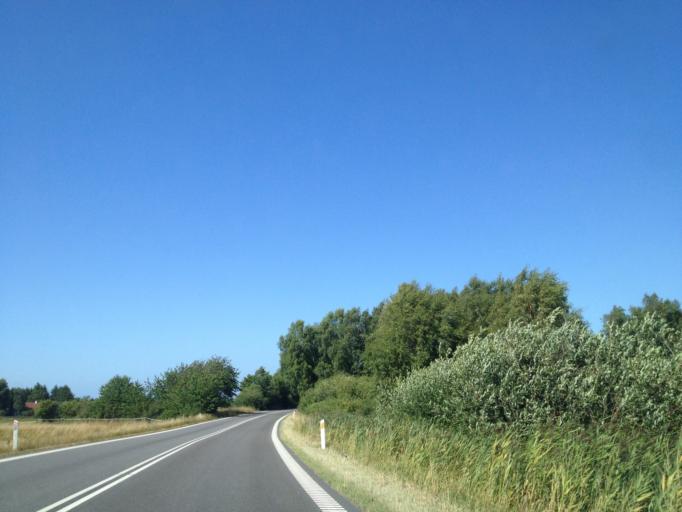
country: DK
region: Capital Region
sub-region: Gribskov Kommune
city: Graested
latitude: 56.0549
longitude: 12.3401
